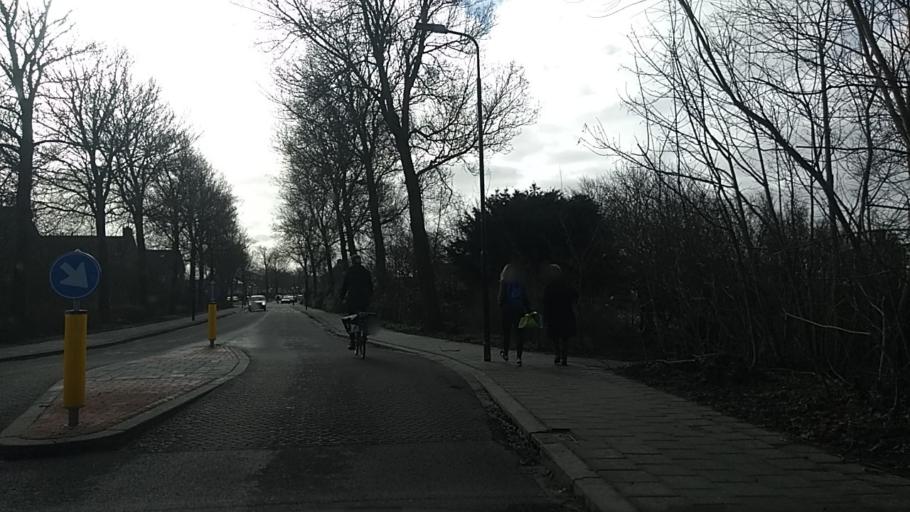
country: NL
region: Friesland
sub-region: Gemeente Harlingen
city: Harlingen
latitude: 53.1702
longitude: 5.4385
